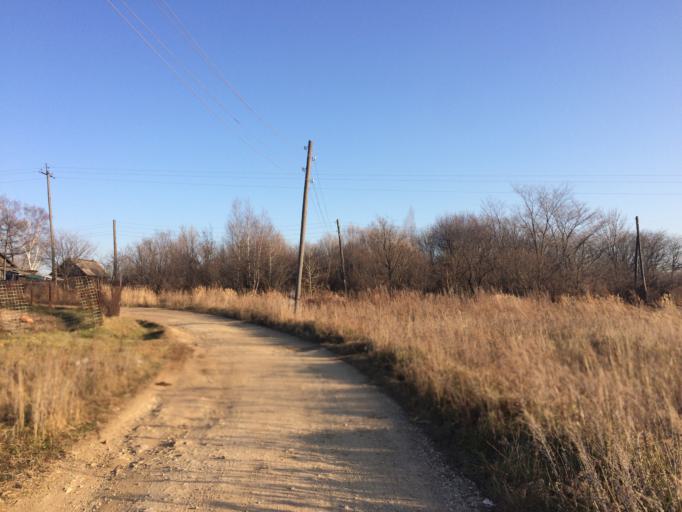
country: RU
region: Primorskiy
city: Ivanovka
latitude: 43.9551
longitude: 132.4682
